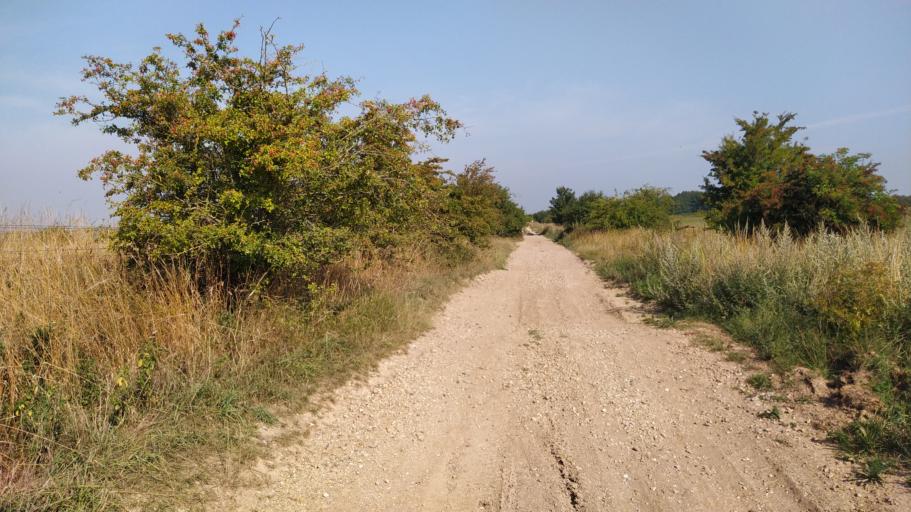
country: GB
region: England
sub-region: Wiltshire
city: Winterbourne Stoke
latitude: 51.1668
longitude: -1.9509
